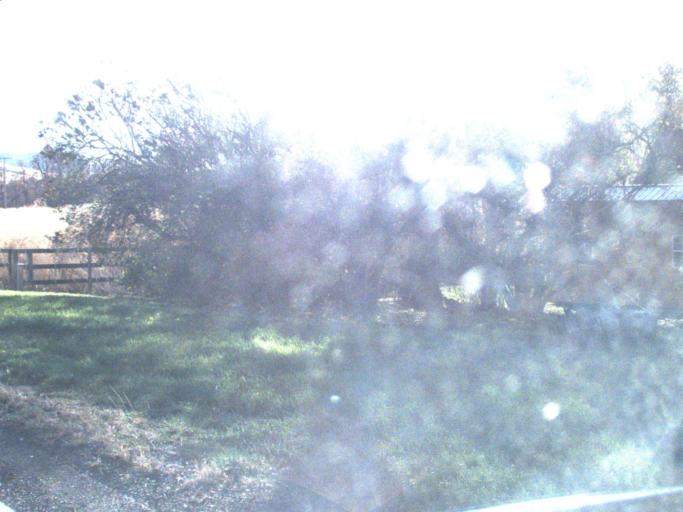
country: US
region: Washington
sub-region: Garfield County
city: Pomeroy
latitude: 46.5209
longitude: -117.8023
